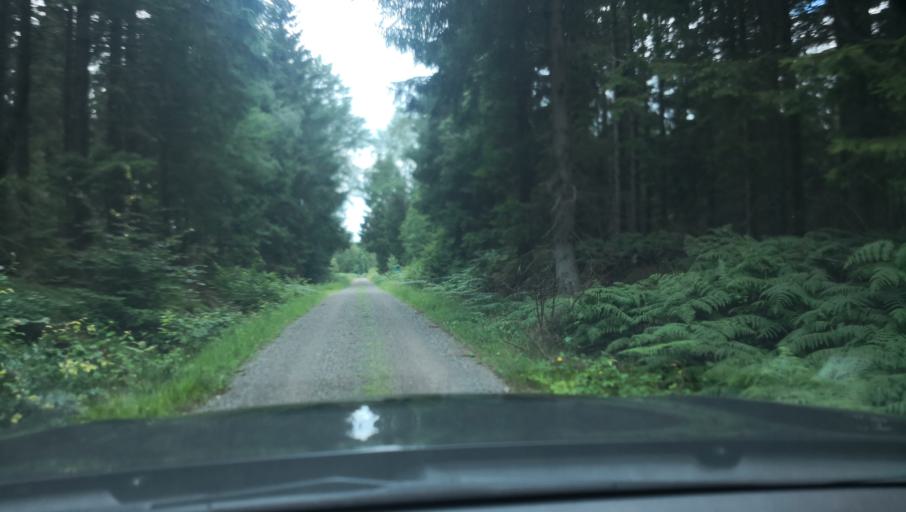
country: SE
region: Skane
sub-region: Simrishamns Kommun
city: Kivik
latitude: 55.6106
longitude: 14.1112
